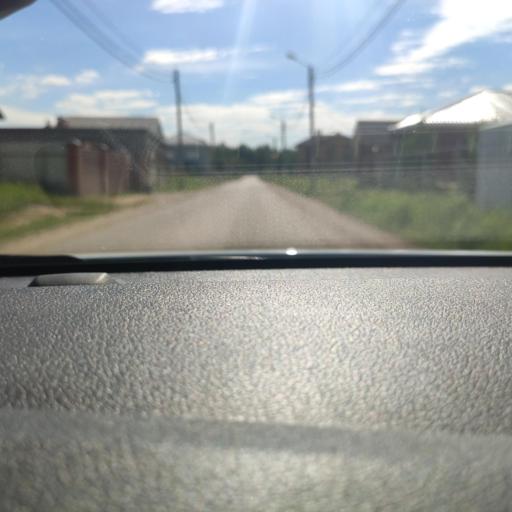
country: RU
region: Tatarstan
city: Vysokaya Gora
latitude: 55.8213
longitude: 49.3104
